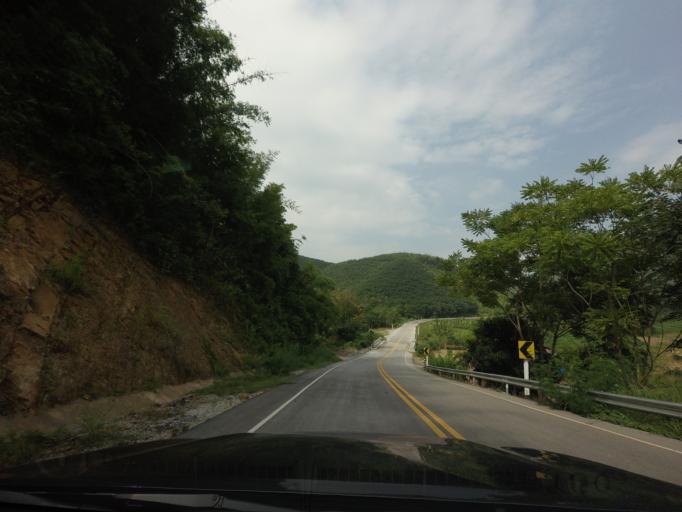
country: LA
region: Xiagnabouli
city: Muang Kenthao
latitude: 17.7736
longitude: 101.5279
